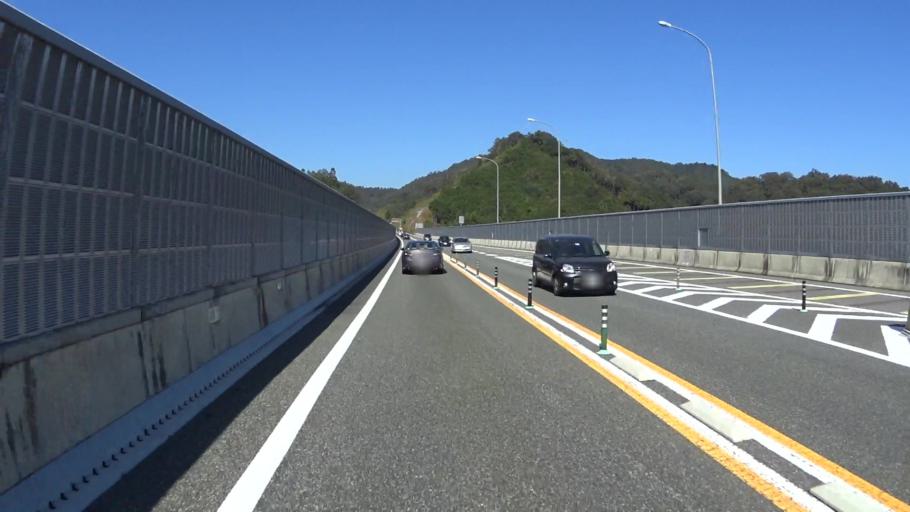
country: JP
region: Kyoto
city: Ayabe
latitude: 35.3376
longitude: 135.3077
